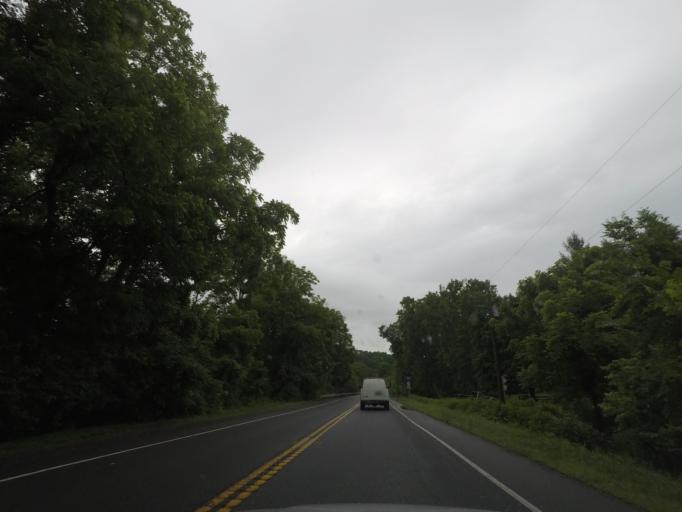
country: US
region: Virginia
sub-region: Loudoun County
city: Brambleton
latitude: 39.0292
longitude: -77.6225
